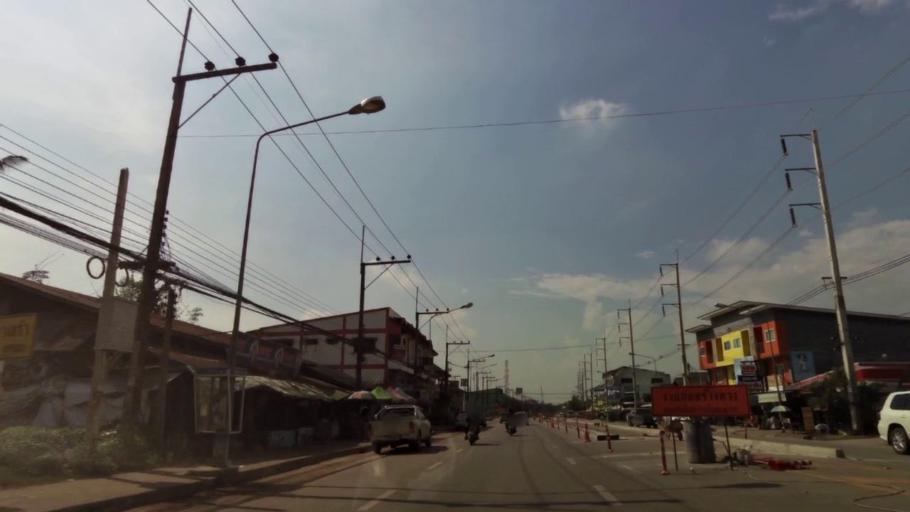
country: TH
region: Chiang Rai
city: Chiang Rai
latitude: 19.8807
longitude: 99.7954
